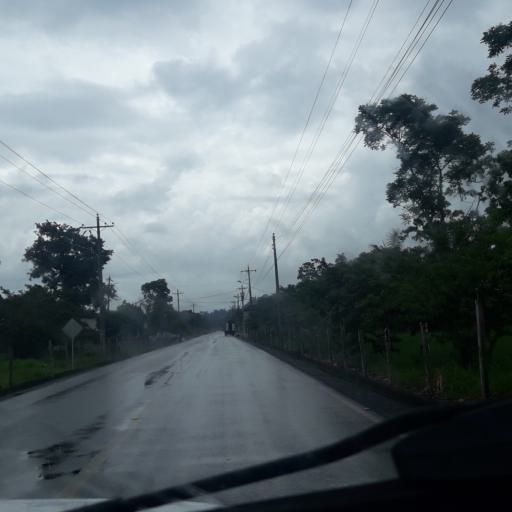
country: EC
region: Napo
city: Tena
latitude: -1.0652
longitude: -77.6472
